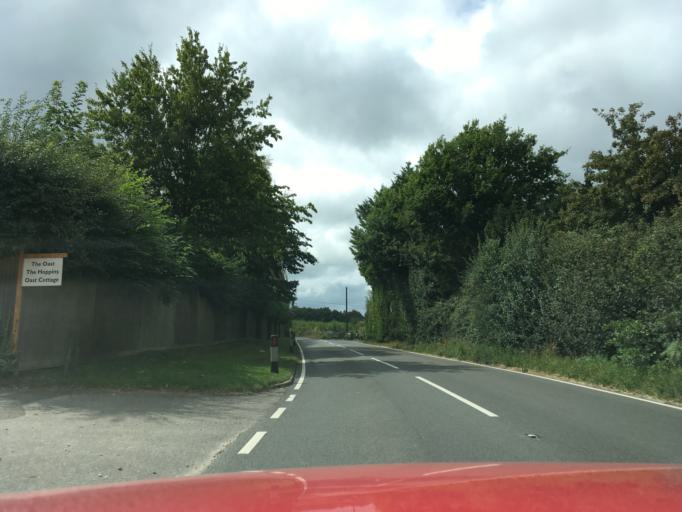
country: GB
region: England
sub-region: Kent
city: Cranbrook
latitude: 51.1107
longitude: 0.5038
